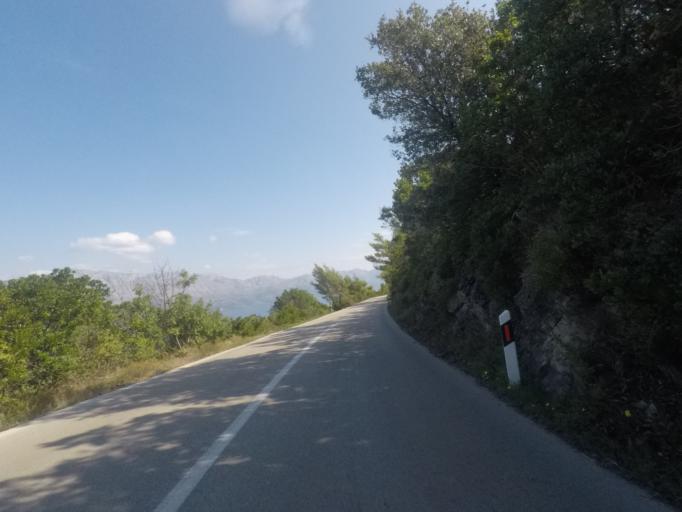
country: HR
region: Dubrovacko-Neretvanska
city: Orebic
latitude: 43.1316
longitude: 17.1294
